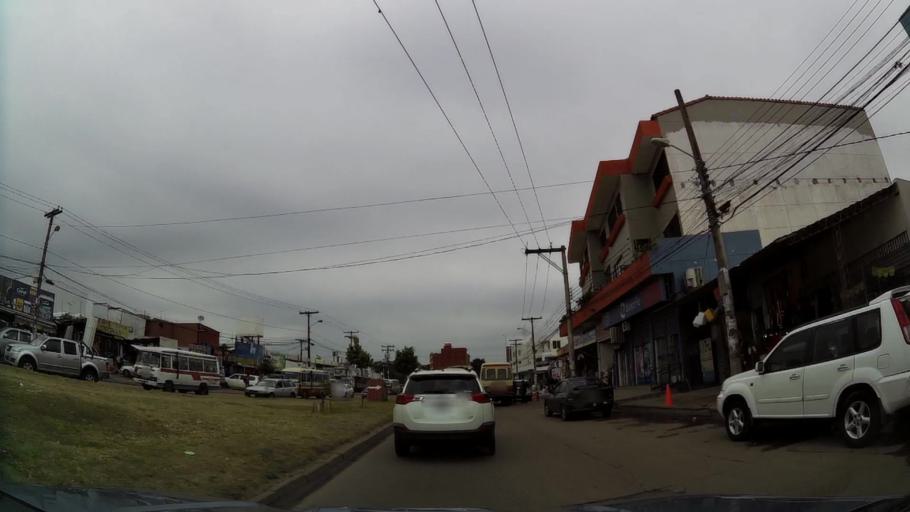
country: BO
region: Santa Cruz
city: Santa Cruz de la Sierra
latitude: -17.7849
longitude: -63.1586
